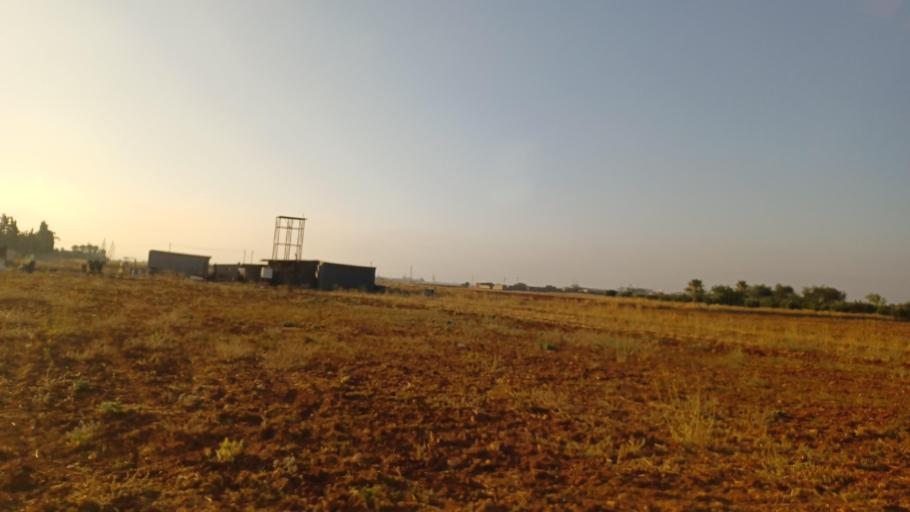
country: CY
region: Ammochostos
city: Avgorou
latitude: 35.0343
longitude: 33.8623
